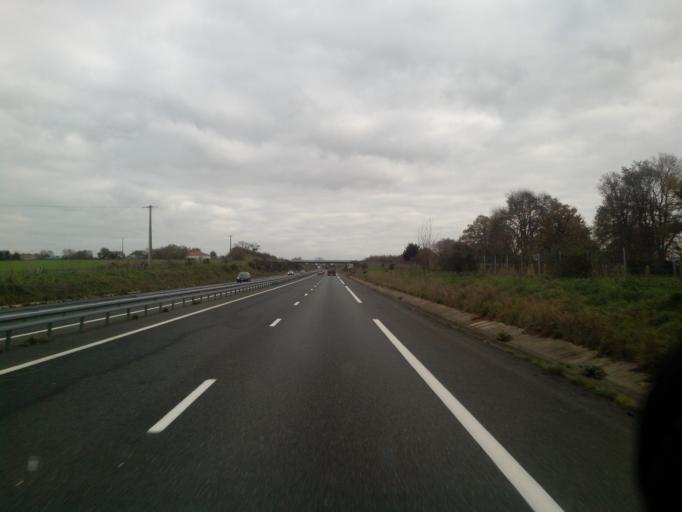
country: FR
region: Poitou-Charentes
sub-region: Departement des Deux-Sevres
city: Saint-Pierre-des-Echaubrognes
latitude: 46.9578
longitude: -0.7803
